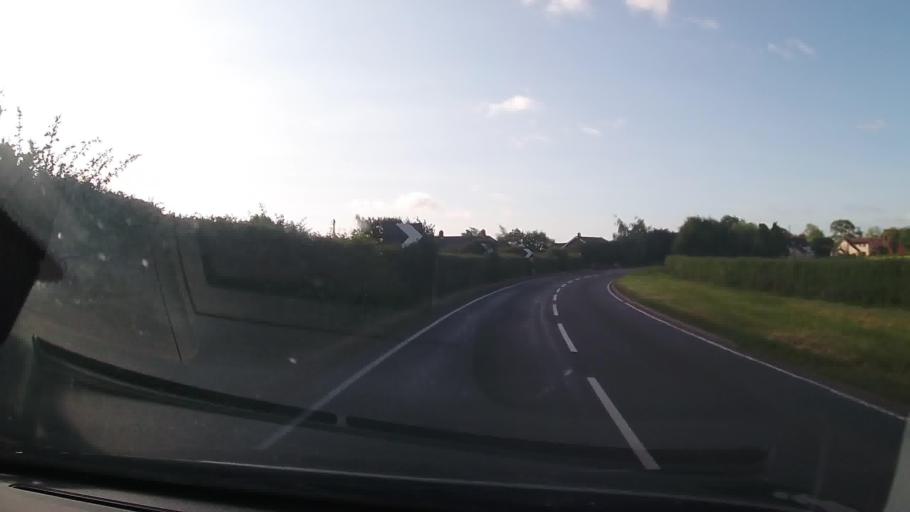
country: GB
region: England
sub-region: Shropshire
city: Withington
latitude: 52.7400
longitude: -2.5734
